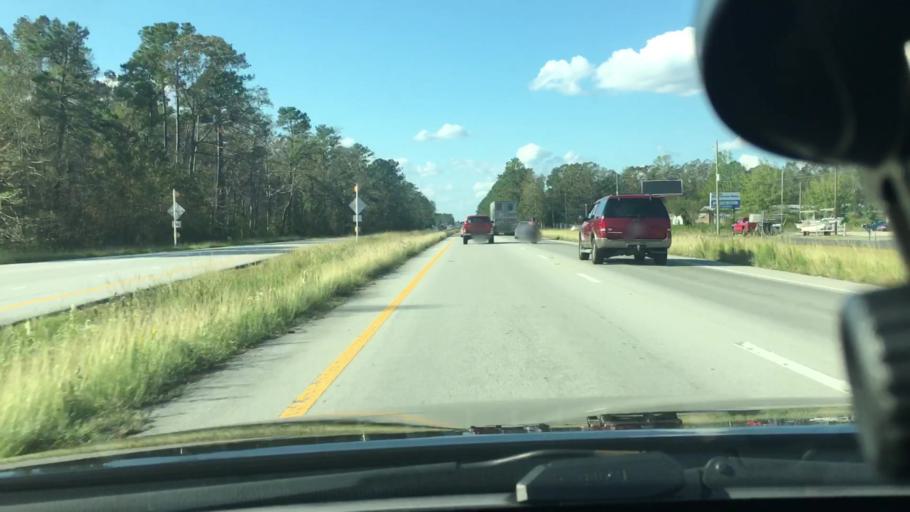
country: US
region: North Carolina
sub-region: Craven County
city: James City
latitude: 35.0387
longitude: -77.0076
